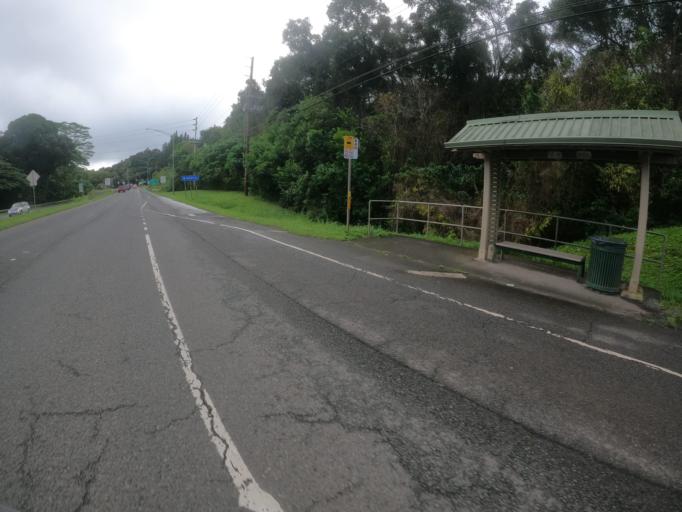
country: US
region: Hawaii
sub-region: Honolulu County
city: Maunawili
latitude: 21.3767
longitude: -157.7827
